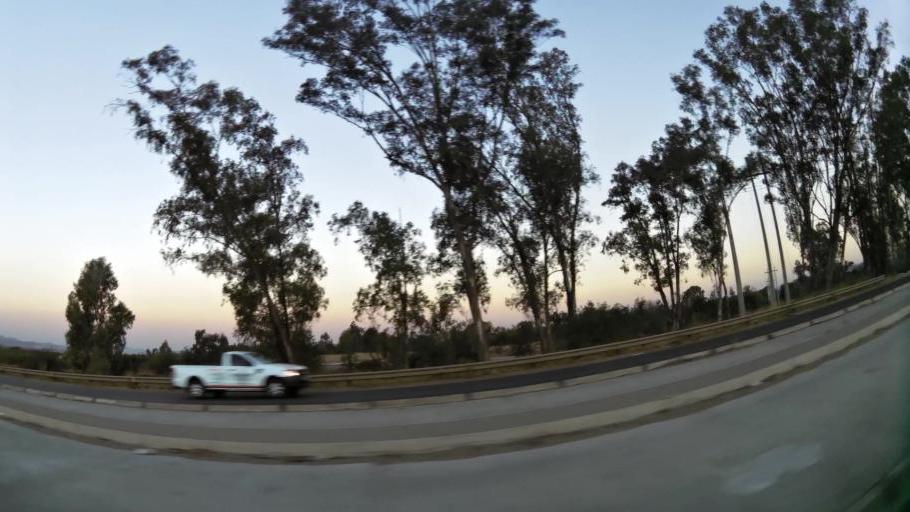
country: ZA
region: North-West
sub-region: Bojanala Platinum District Municipality
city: Rustenburg
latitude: -25.6455
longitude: 27.2579
